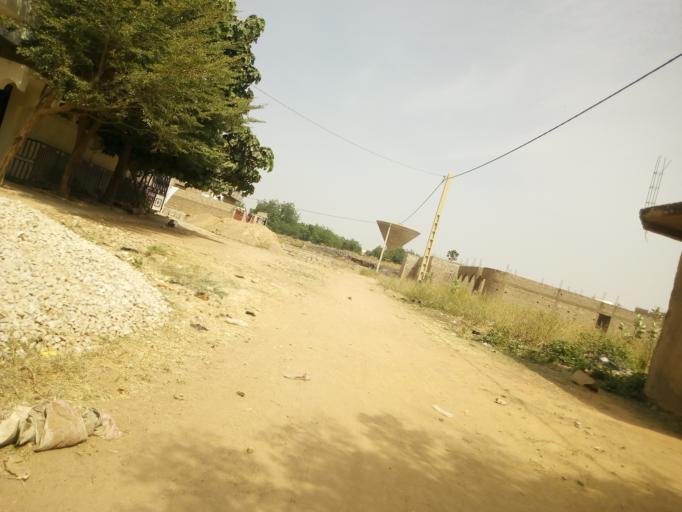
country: ML
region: Kayes
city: Kayes
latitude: 14.4351
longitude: -11.4368
